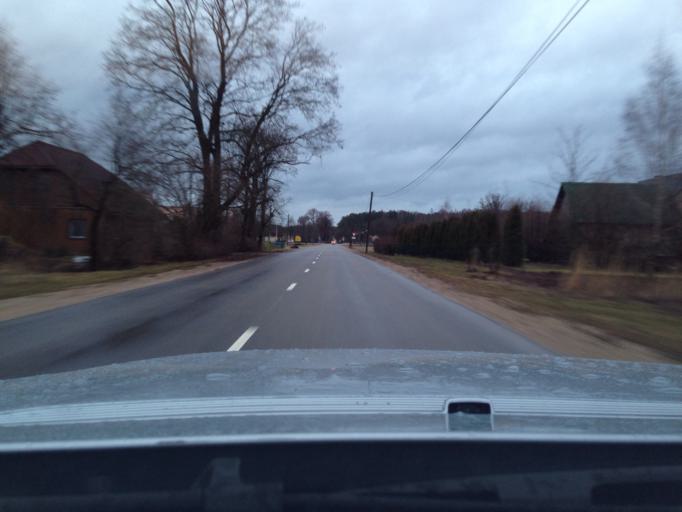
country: LV
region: Marupe
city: Marupe
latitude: 56.8811
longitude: 23.9791
